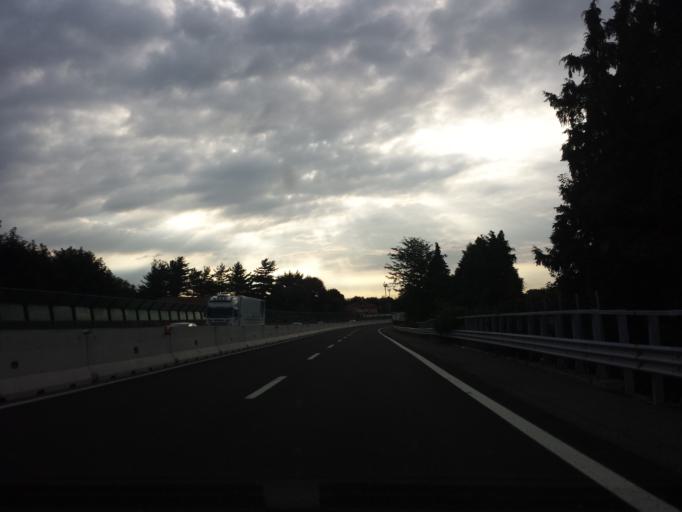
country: IT
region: Lombardy
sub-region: Provincia di Varese
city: Vergiate
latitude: 45.7199
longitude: 8.6956
